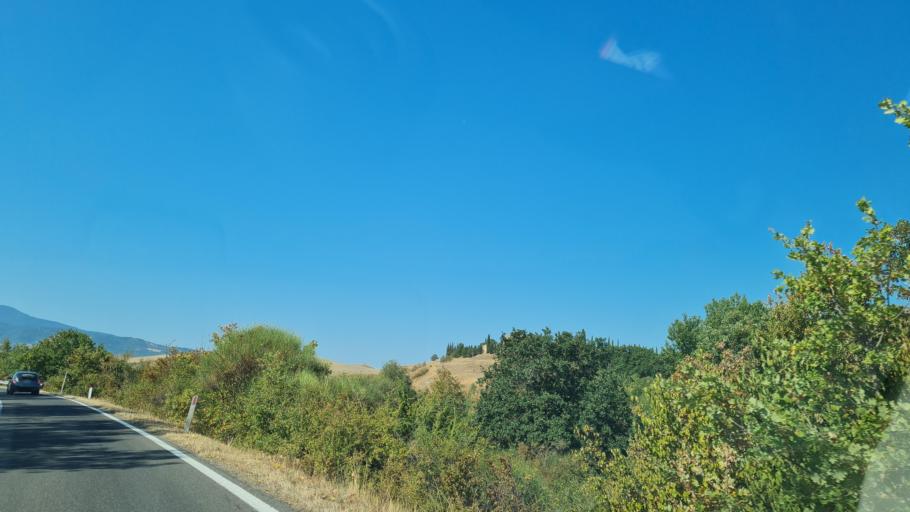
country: IT
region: Tuscany
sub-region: Provincia di Siena
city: Chianciano Terme
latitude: 43.0064
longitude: 11.7313
